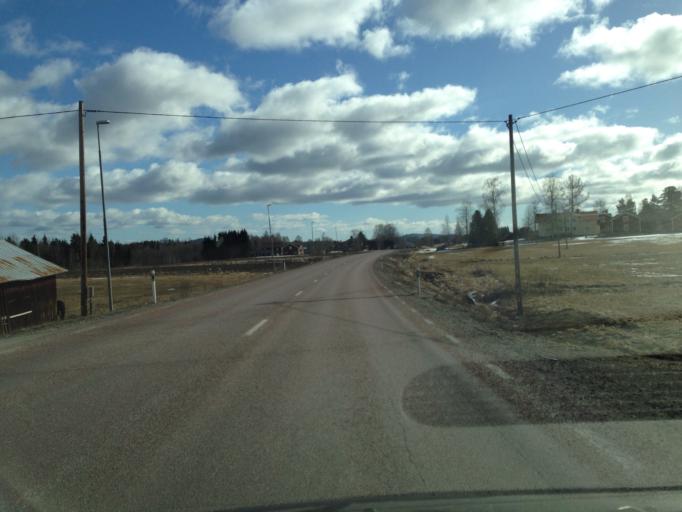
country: SE
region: Gaevleborg
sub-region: Ljusdals Kommun
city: Farila
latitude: 61.7996
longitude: 15.8106
